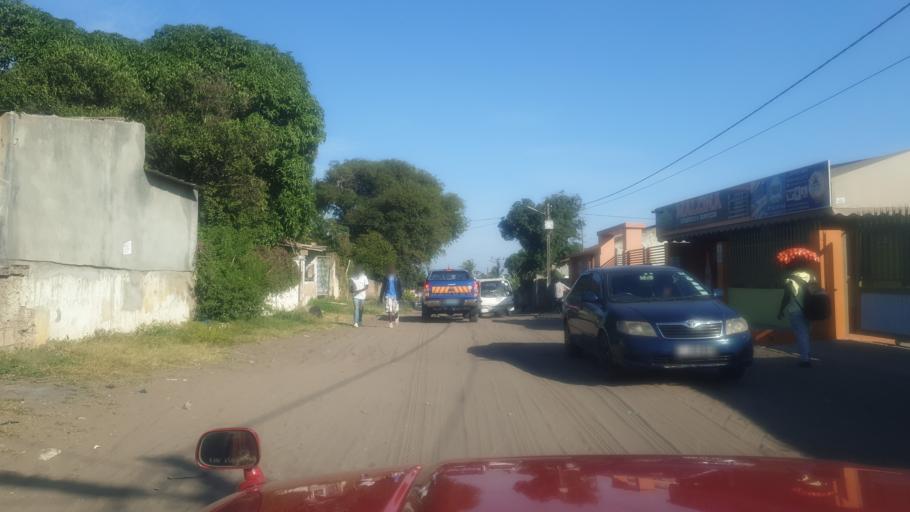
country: MZ
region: Maputo City
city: Maputo
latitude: -25.9124
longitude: 32.5610
